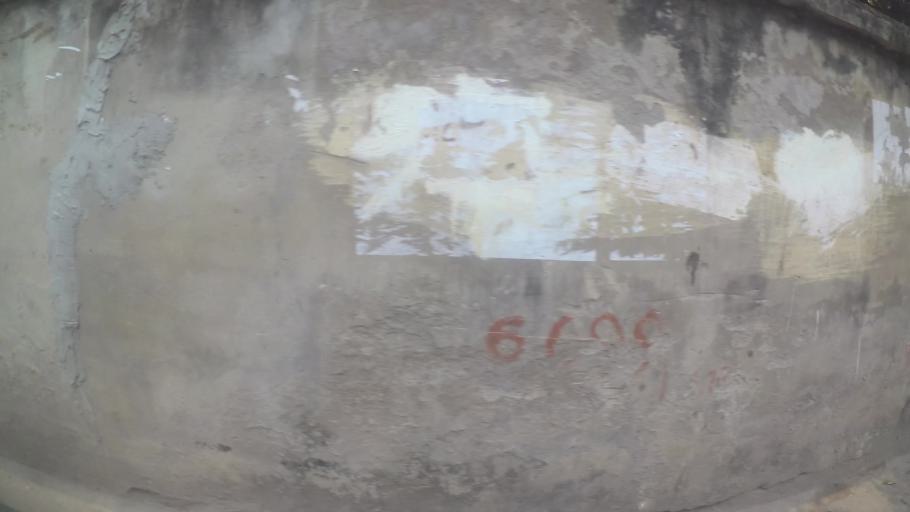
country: VN
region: Ha Noi
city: Ha Dong
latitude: 20.9832
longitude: 105.7488
